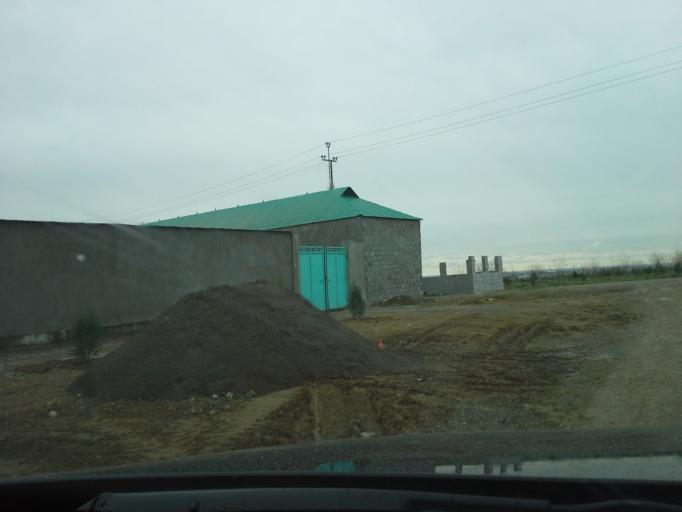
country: TM
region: Ahal
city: Abadan
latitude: 37.9607
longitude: 58.2314
